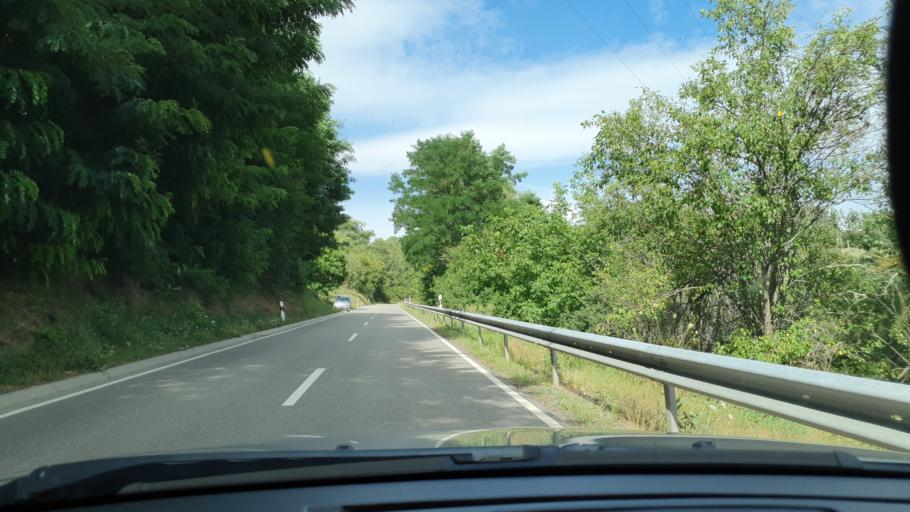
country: DE
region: Rheinland-Pfalz
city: Thaleischweiler-Froschen
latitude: 49.2694
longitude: 7.5826
